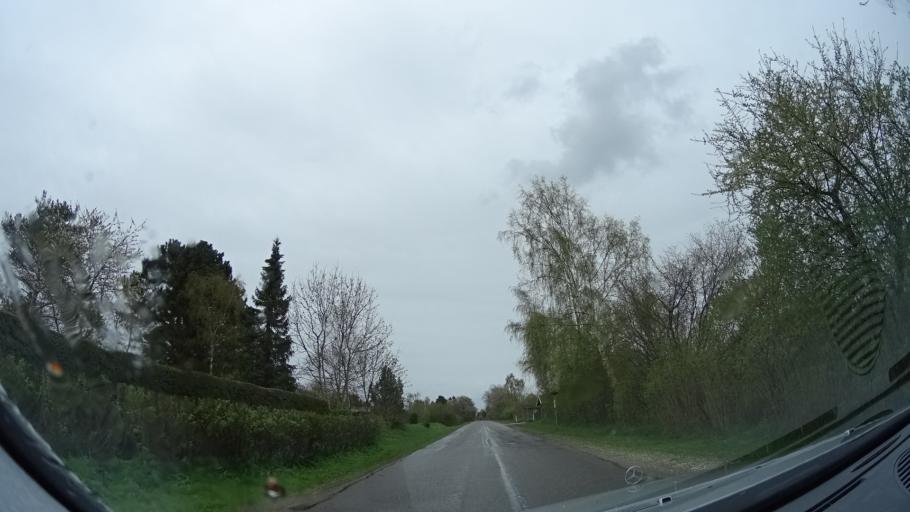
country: DK
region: Zealand
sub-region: Lejre Kommune
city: Ejby
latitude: 55.7085
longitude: 11.8478
